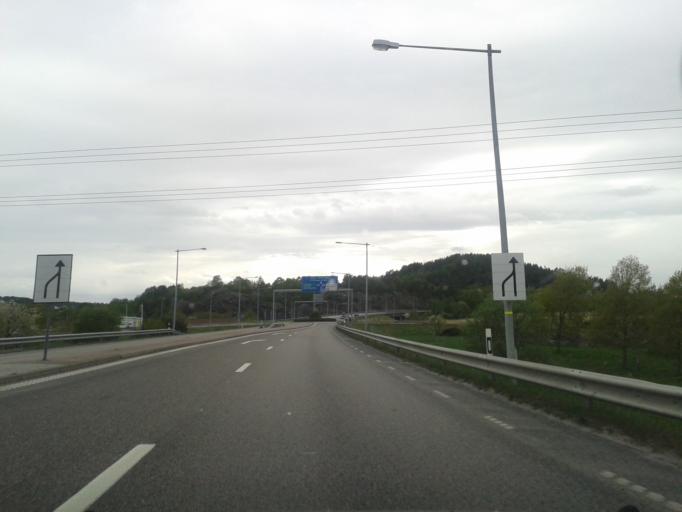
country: SE
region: Vaestra Goetaland
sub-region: Stenungsunds Kommun
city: Stora Hoga
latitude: 58.0251
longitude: 11.8455
